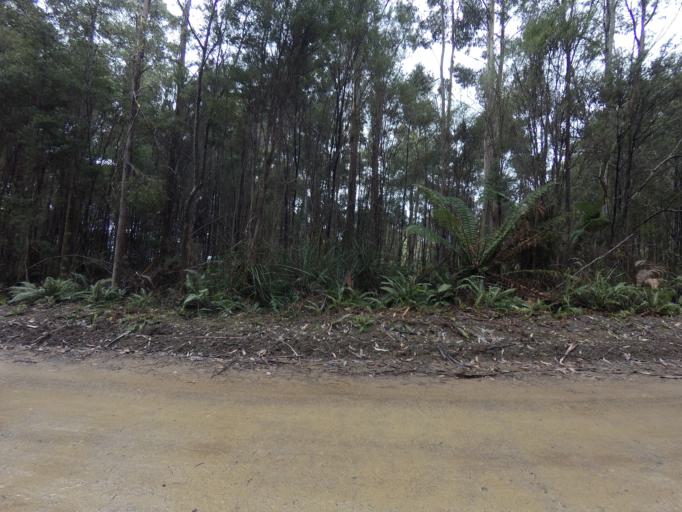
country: AU
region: Tasmania
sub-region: Huon Valley
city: Geeveston
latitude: -43.5496
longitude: 146.8869
